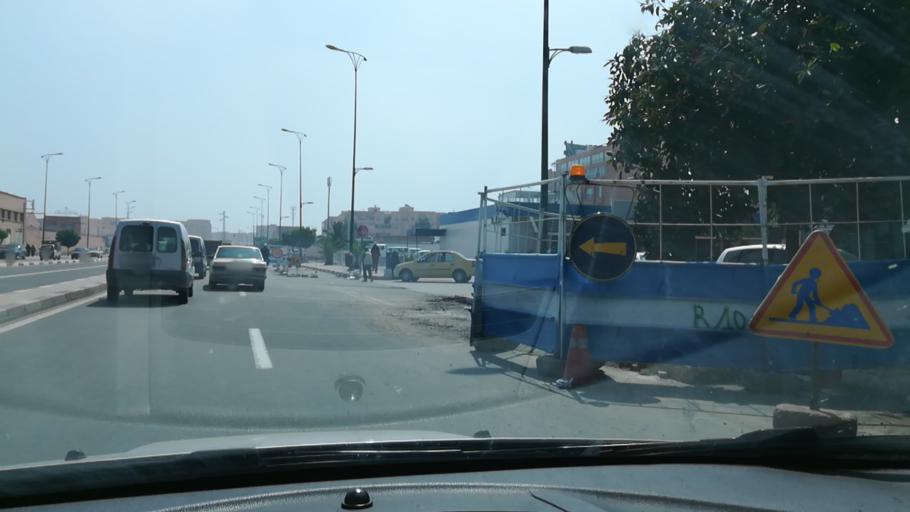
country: MA
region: Marrakech-Tensift-Al Haouz
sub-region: Marrakech
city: Marrakesh
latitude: 31.6268
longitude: -8.0306
